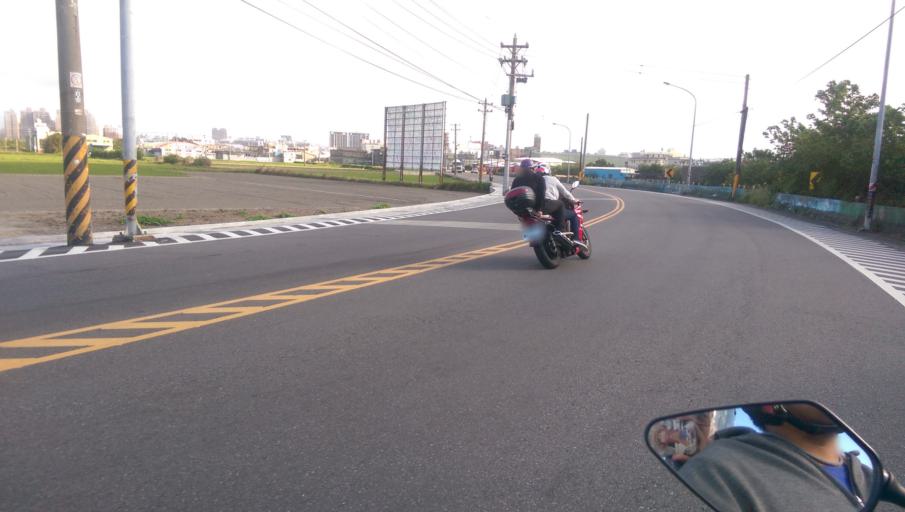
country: TW
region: Taiwan
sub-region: Hsinchu
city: Hsinchu
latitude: 24.8292
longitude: 120.9544
